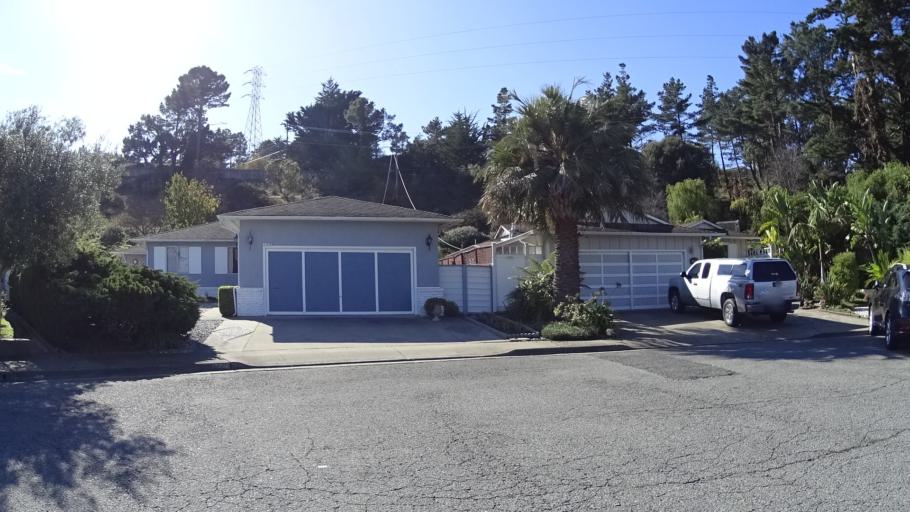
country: US
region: California
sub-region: San Mateo County
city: Pacifica
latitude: 37.6361
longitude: -122.4556
